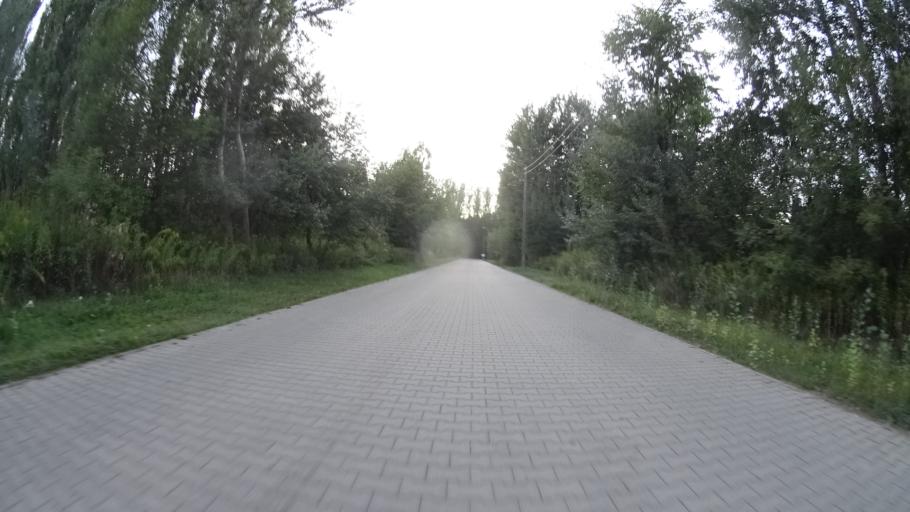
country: PL
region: Masovian Voivodeship
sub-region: Powiat warszawski zachodni
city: Ozarow Mazowiecki
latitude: 52.2267
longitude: 20.7709
